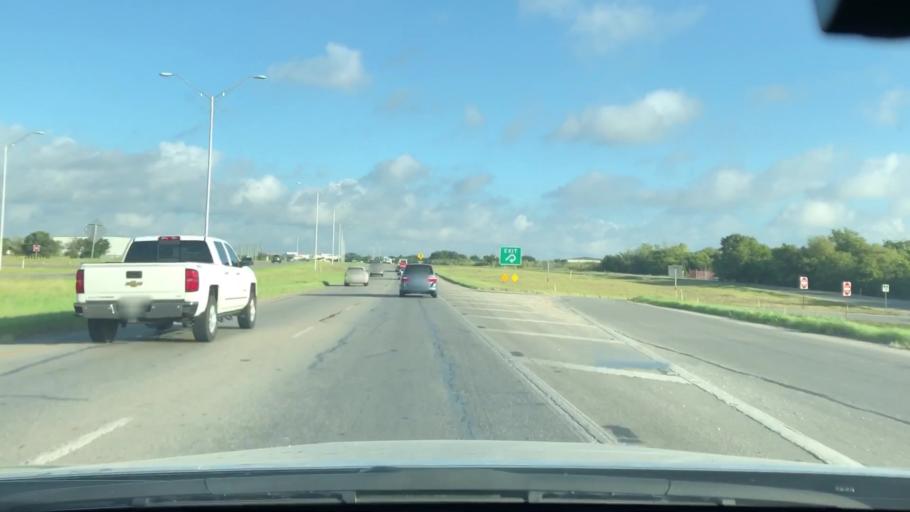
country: US
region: Texas
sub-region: Bexar County
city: Universal City
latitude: 29.5374
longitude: -98.3064
